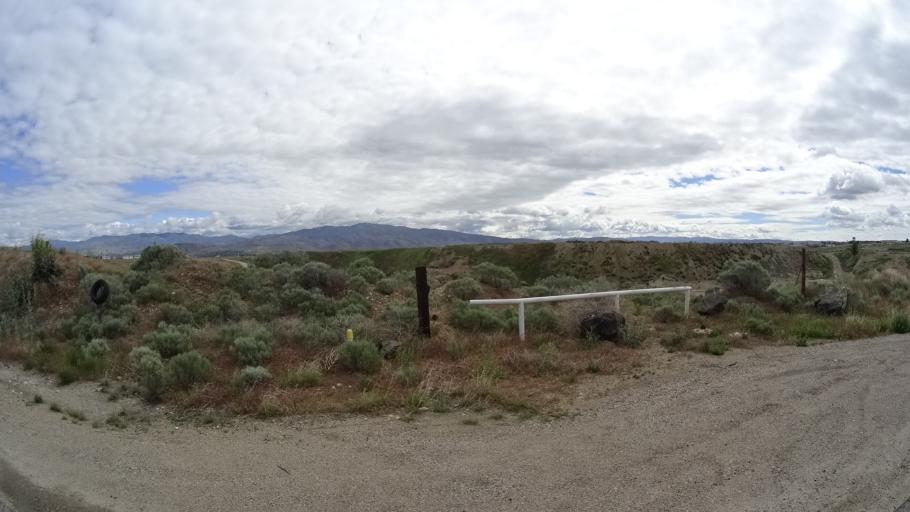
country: US
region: Idaho
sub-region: Ada County
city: Boise
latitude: 43.5539
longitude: -116.1869
